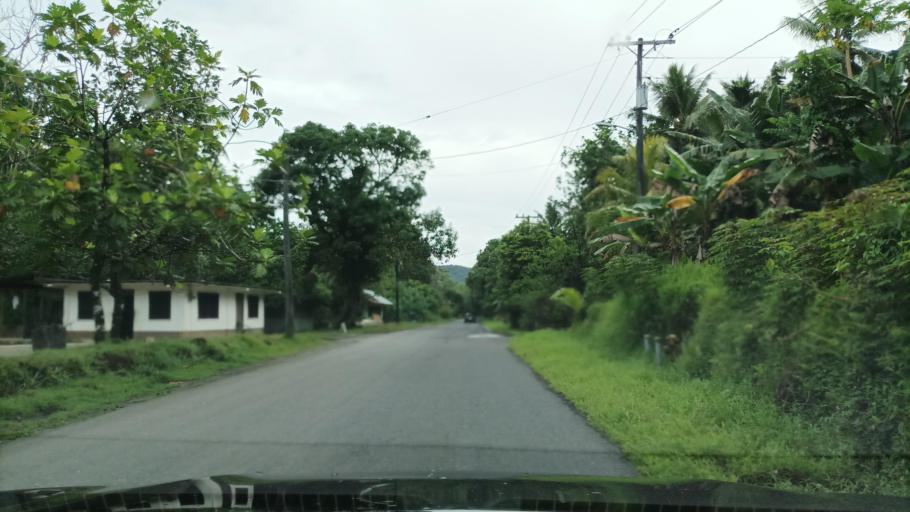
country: FM
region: Pohnpei
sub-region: Kolonia Municipality
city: Kolonia
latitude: 6.9385
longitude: 158.2782
